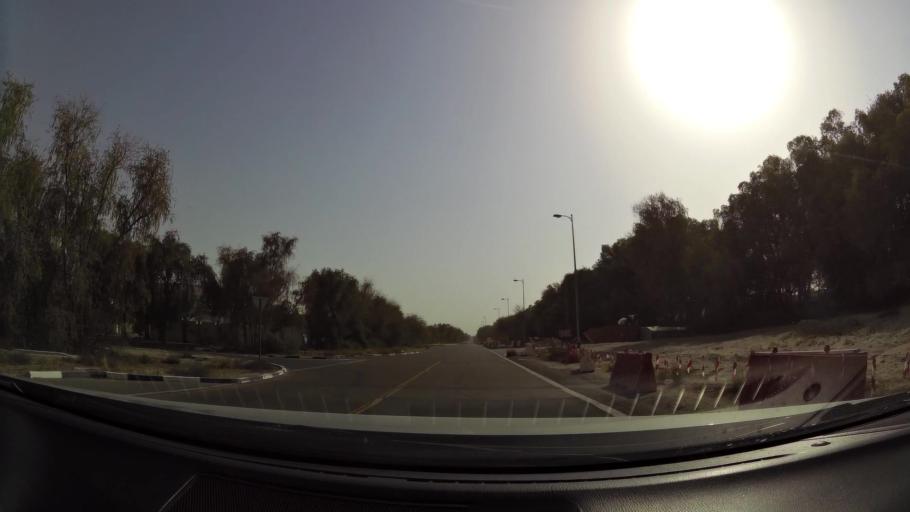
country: AE
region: Dubai
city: Dubai
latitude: 25.1551
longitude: 55.3216
